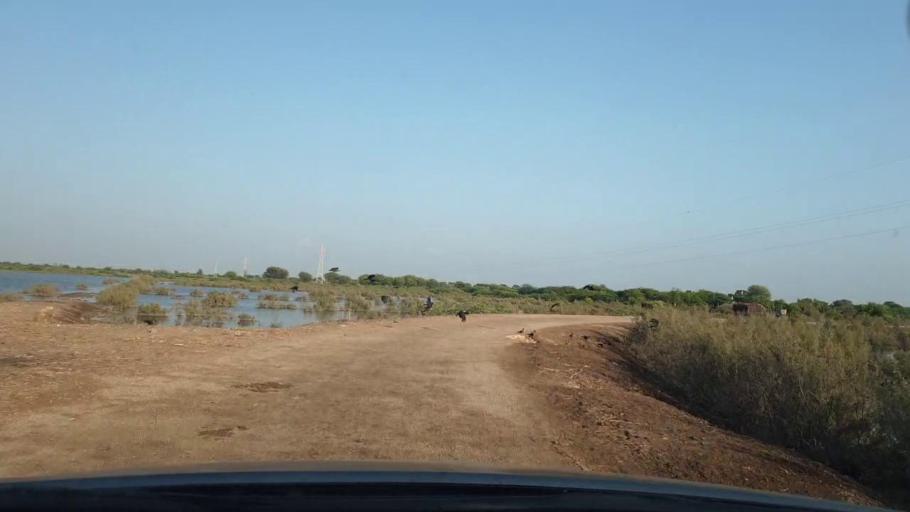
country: PK
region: Sindh
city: Naukot
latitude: 24.7698
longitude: 69.2021
